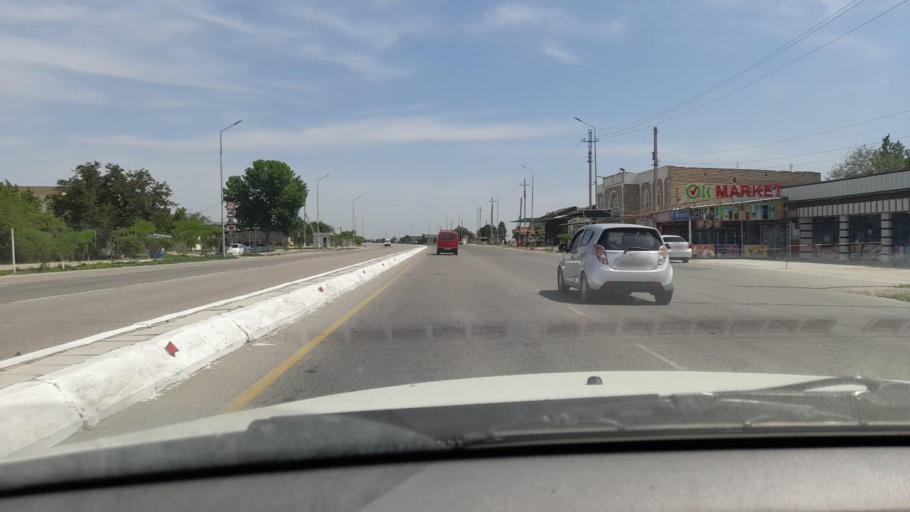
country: UZ
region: Bukhara
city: Galaosiyo
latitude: 39.8649
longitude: 64.4481
